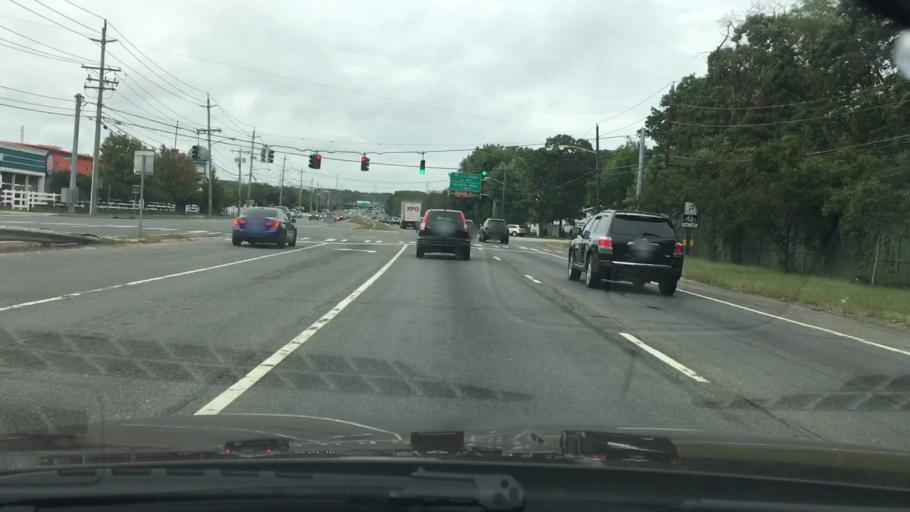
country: US
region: New York
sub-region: Suffolk County
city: Islandia
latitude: 40.8029
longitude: -73.1768
